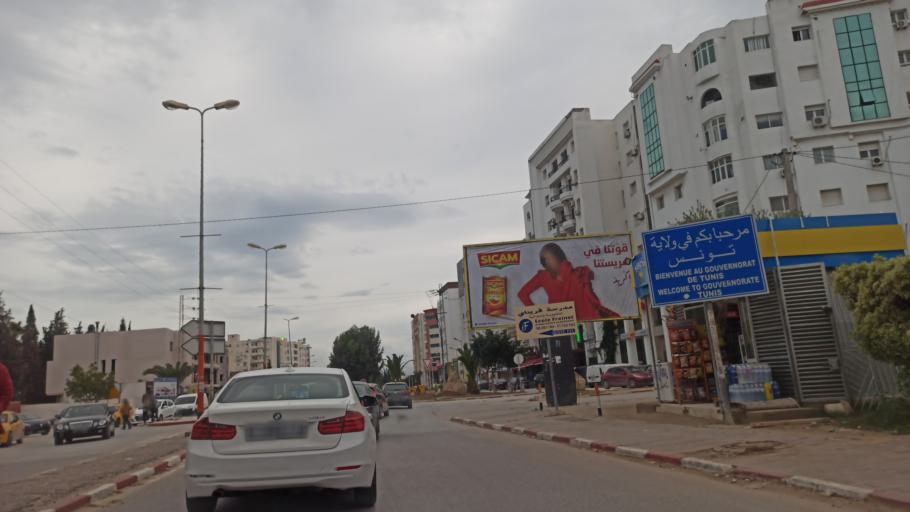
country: TN
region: Ariana
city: Ariana
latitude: 36.8621
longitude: 10.2541
